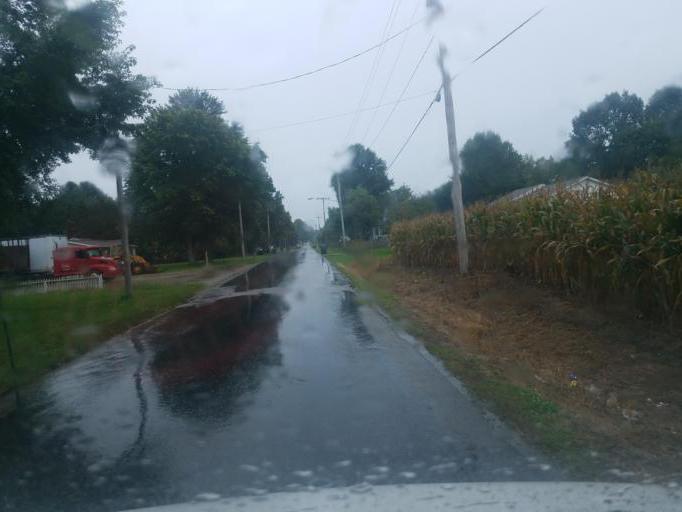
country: US
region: Ohio
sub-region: Wayne County
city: Creston
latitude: 40.9859
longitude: -81.8891
